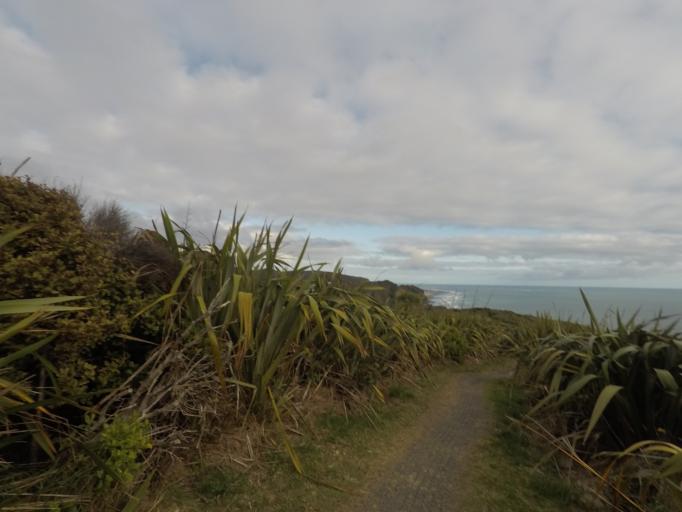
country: NZ
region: Auckland
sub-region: Auckland
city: Muriwai Beach
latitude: -36.9738
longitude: 174.4680
